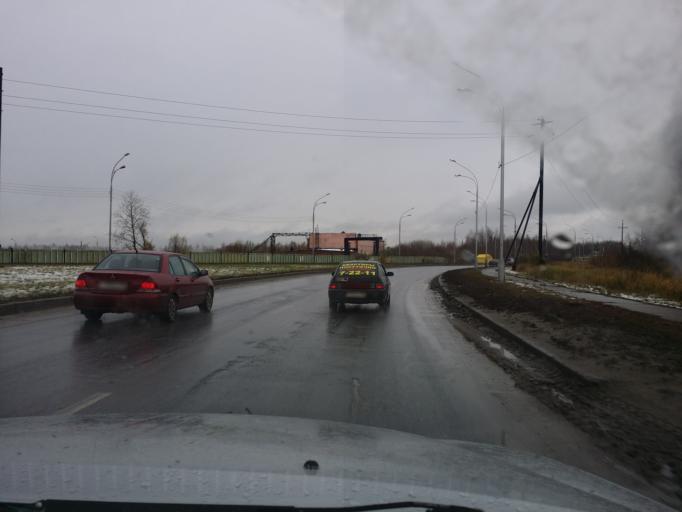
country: RU
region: Khanty-Mansiyskiy Avtonomnyy Okrug
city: Nizhnevartovsk
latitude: 60.9701
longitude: 76.5303
